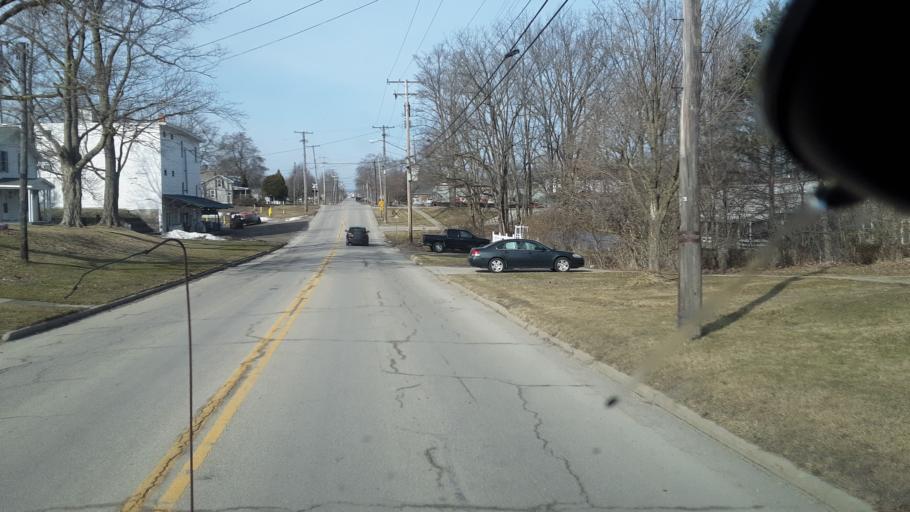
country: US
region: Ohio
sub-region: Ashtabula County
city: Jefferson
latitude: 41.7384
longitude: -80.7595
